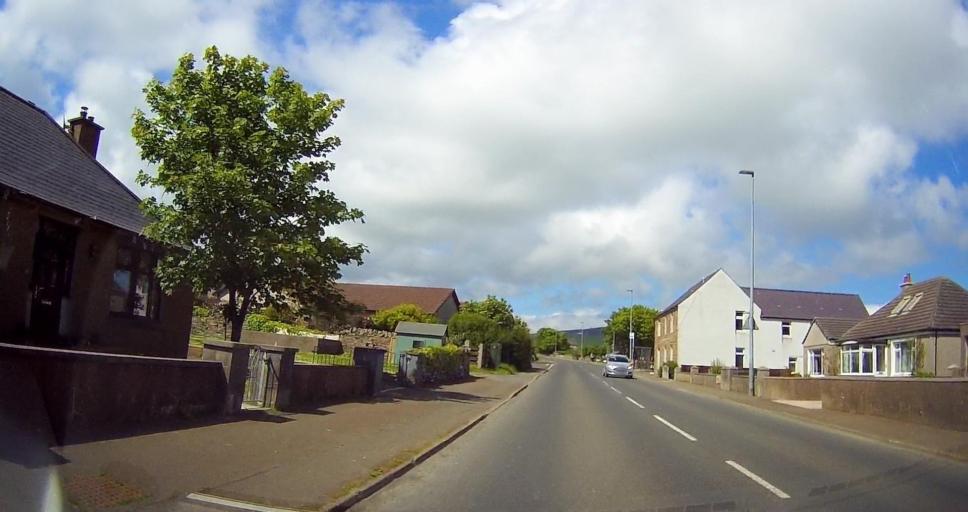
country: GB
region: Scotland
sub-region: Orkney Islands
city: Orkney
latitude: 58.9777
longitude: -2.9712
